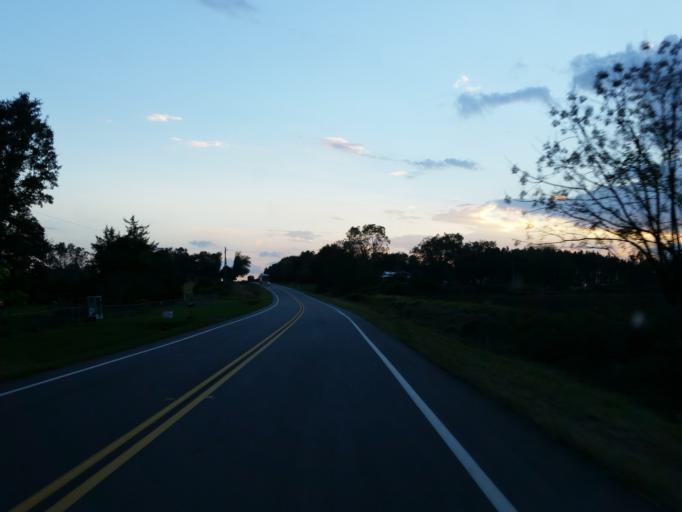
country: US
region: Georgia
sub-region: Pulaski County
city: Hawkinsville
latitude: 32.2540
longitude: -83.4934
